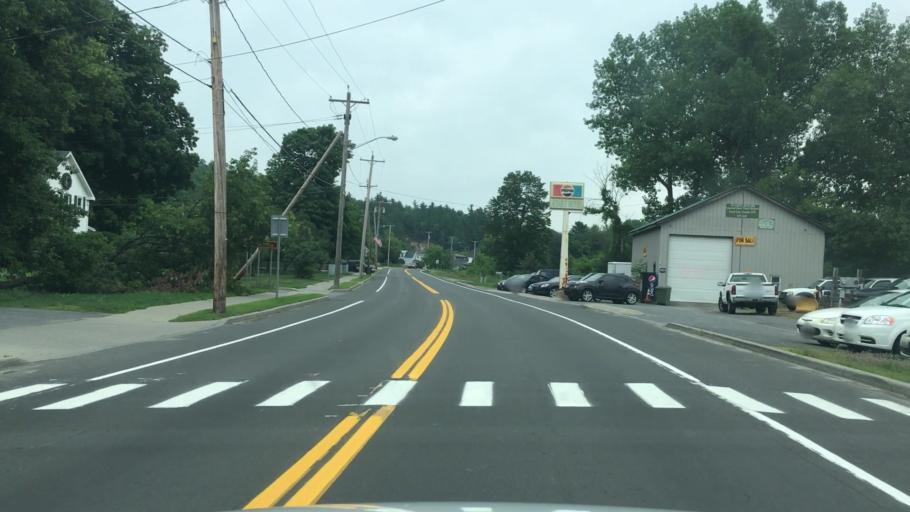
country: US
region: New York
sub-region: Clinton County
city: Peru
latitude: 44.4417
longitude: -73.6734
